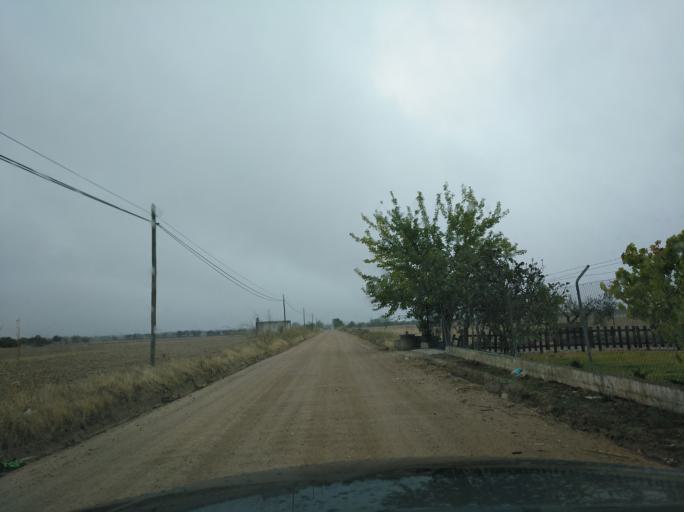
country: PT
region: Portalegre
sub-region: Campo Maior
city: Campo Maior
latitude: 38.9631
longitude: -7.0722
